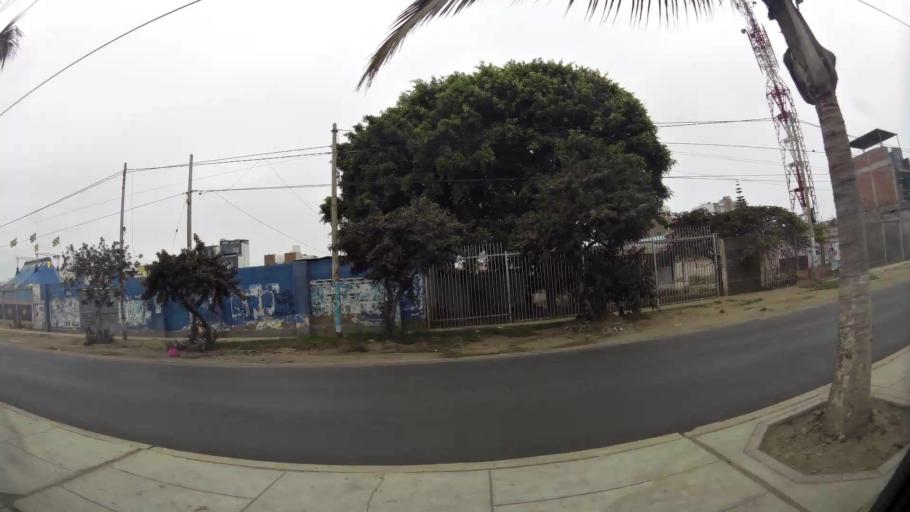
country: PE
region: La Libertad
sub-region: Provincia de Trujillo
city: Buenos Aires
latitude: -8.1320
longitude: -79.0452
